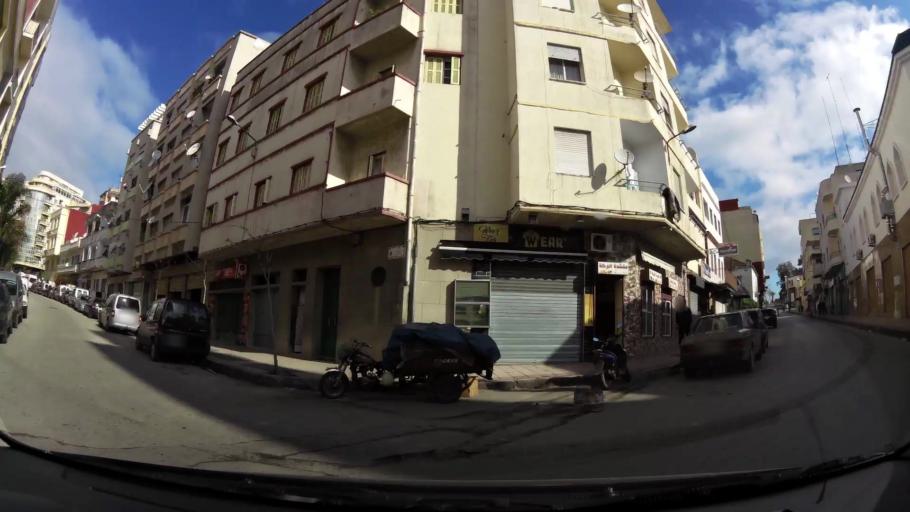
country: MA
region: Tanger-Tetouan
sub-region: Tanger-Assilah
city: Tangier
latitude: 35.7787
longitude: -5.8187
